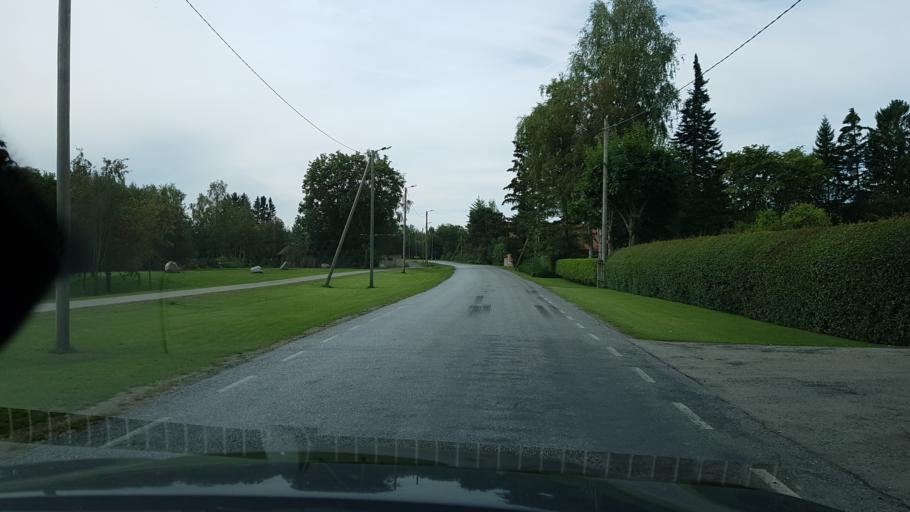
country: EE
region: Harju
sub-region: Raasiku vald
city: Raasiku
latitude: 59.4457
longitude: 25.1732
